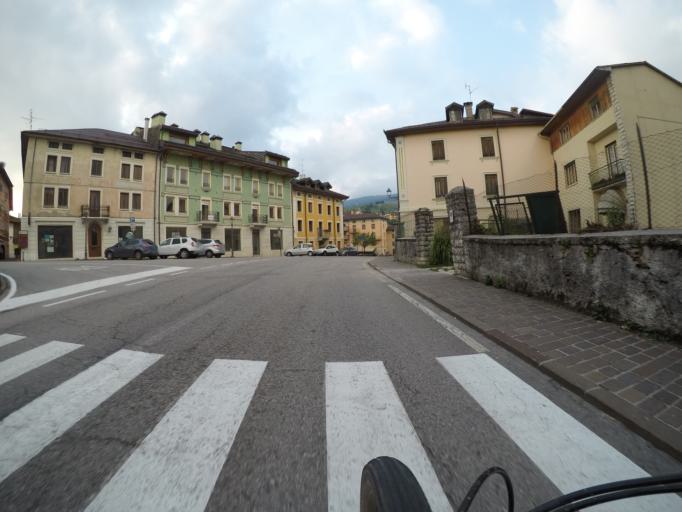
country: IT
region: Veneto
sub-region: Provincia di Vicenza
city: Gallio
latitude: 45.8918
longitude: 11.5479
